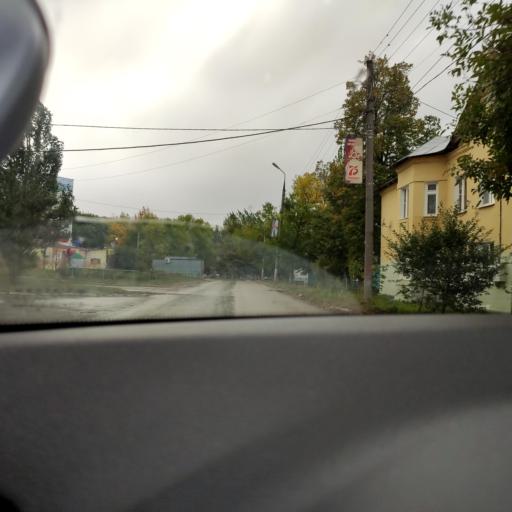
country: RU
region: Samara
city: Novosemeykino
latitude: 53.3705
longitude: 50.3579
